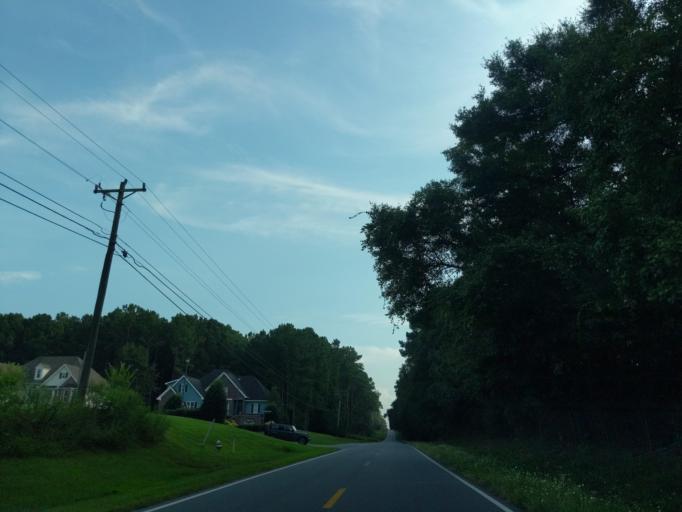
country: US
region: Georgia
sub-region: Thomas County
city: Thomasville
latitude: 30.8967
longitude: -83.9468
